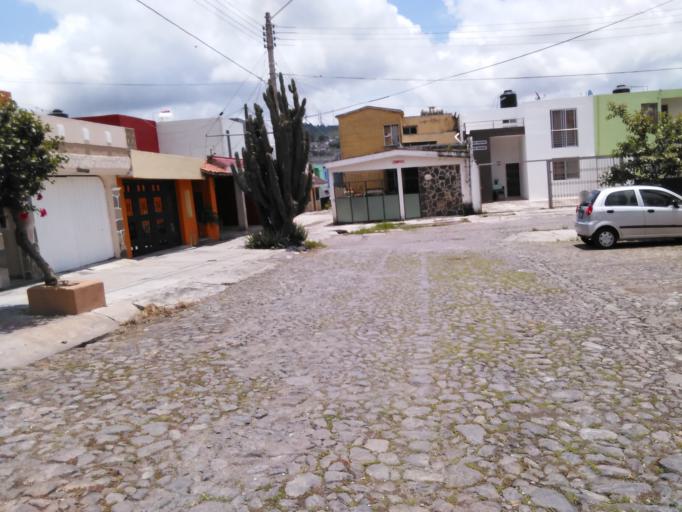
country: MX
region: Nayarit
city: Tepic
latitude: 21.5170
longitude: -104.9177
